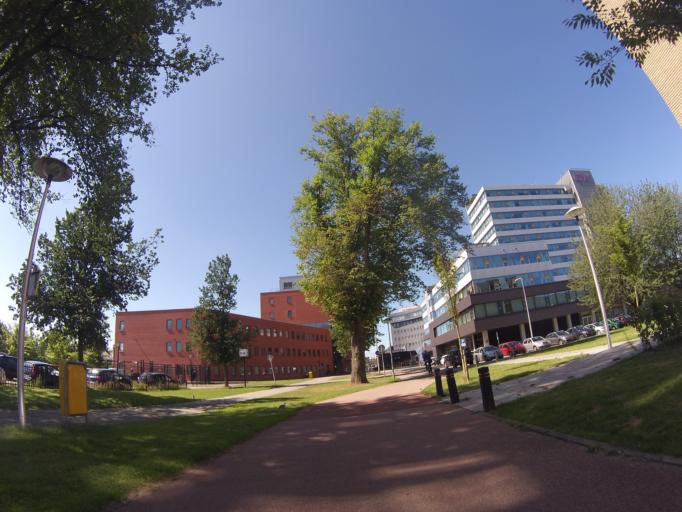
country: NL
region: Utrecht
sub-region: Gemeente Utrecht
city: Utrecht
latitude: 52.1111
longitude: 5.1267
